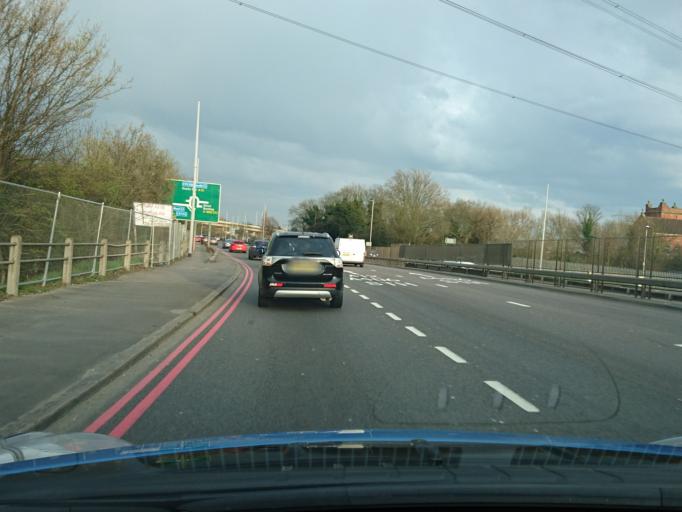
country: GB
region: England
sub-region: Greater London
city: Woodford Green
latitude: 51.5764
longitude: 0.0394
